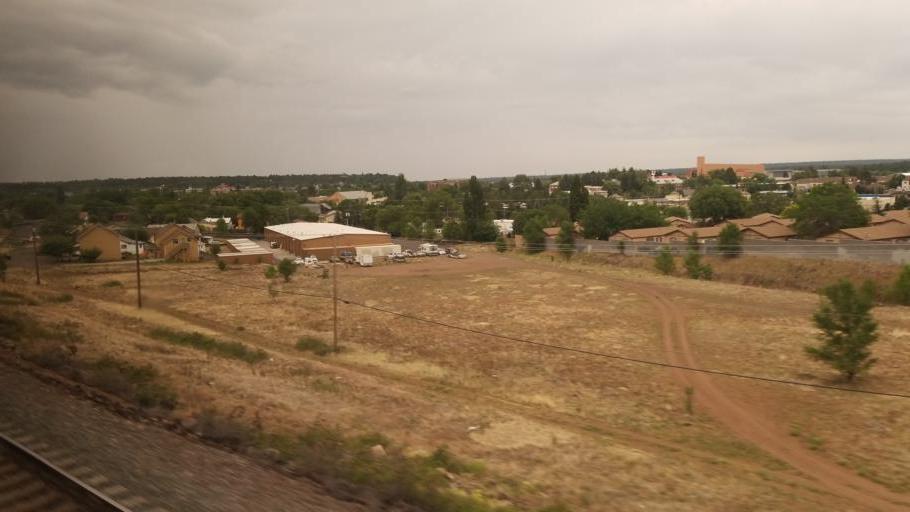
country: US
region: Arizona
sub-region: Coconino County
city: Flagstaff
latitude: 35.1948
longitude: -111.6643
